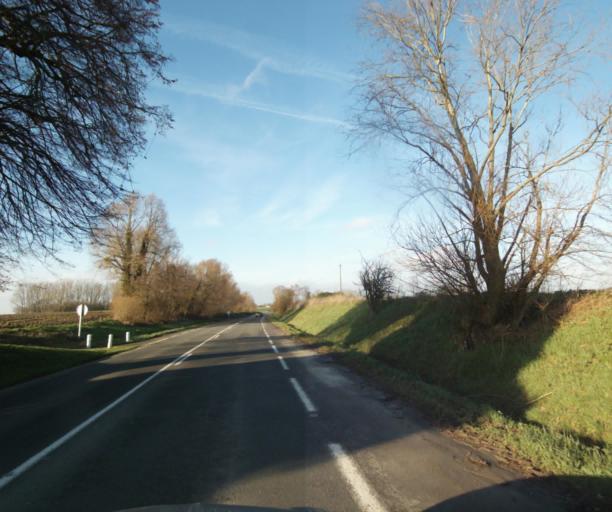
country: FR
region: Nord-Pas-de-Calais
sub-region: Departement du Nord
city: Preseau
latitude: 50.3189
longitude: 3.5675
